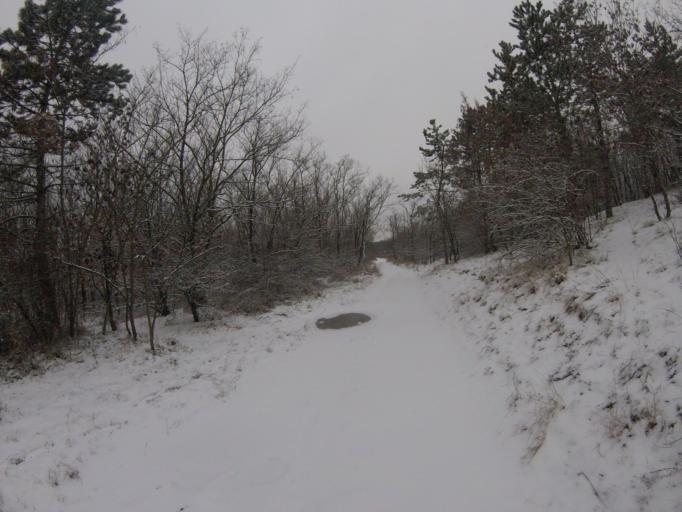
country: HU
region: Fejer
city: Pakozd
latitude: 47.2257
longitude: 18.5315
